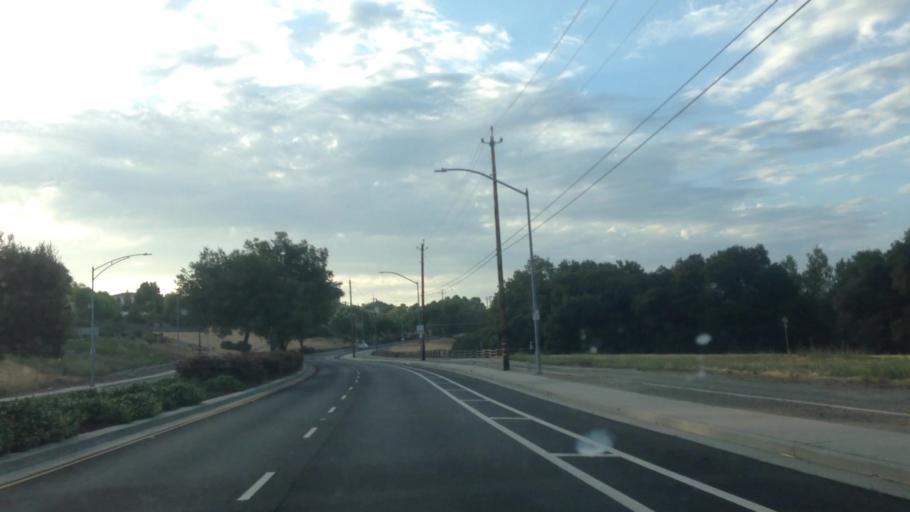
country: US
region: California
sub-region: Santa Clara County
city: Seven Trees
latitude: 37.2971
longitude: -121.7935
